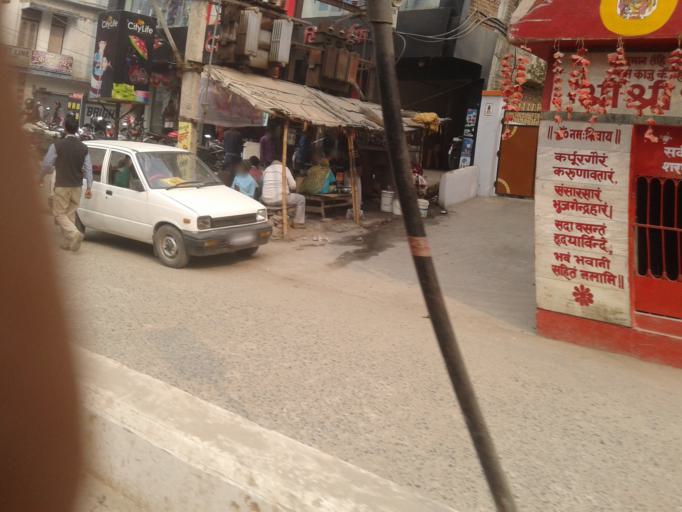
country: IN
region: Bihar
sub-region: Muzaffarpur
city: Muzaffarpur
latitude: 26.1106
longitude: 85.3960
